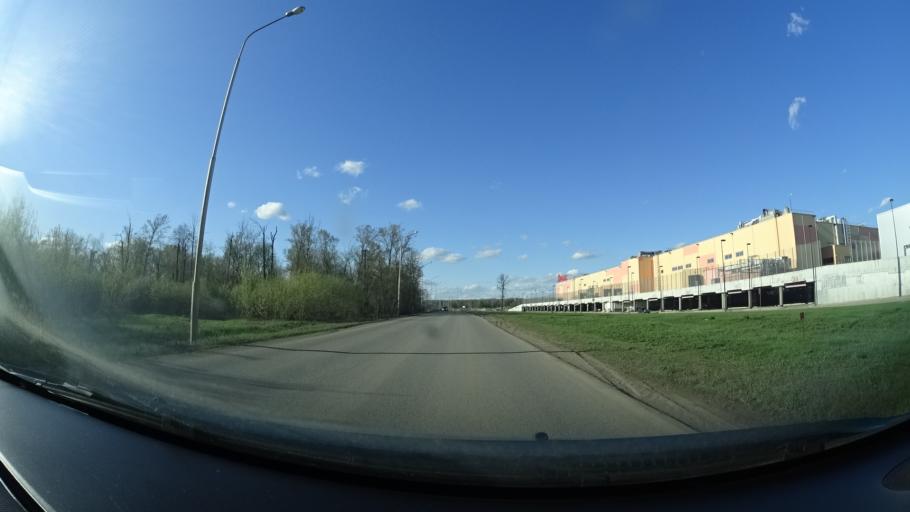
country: RU
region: Bashkortostan
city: Ufa
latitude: 54.6733
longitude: 55.9256
